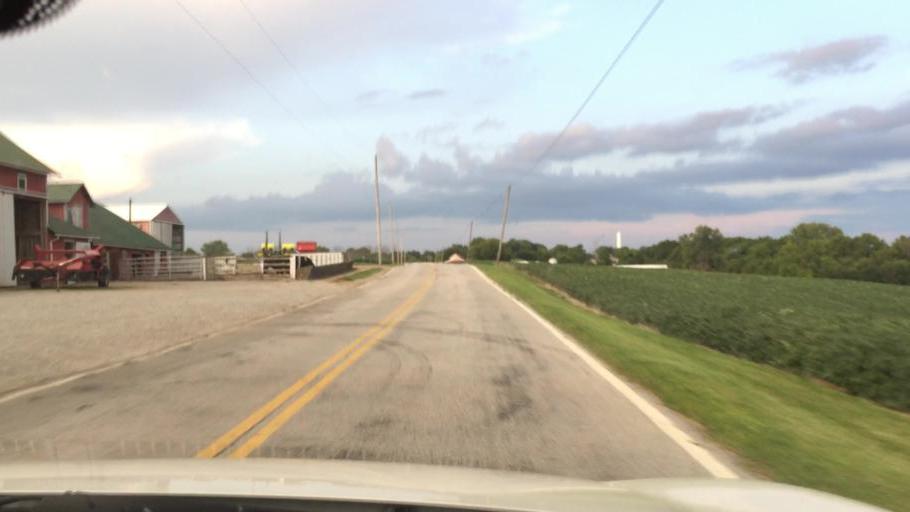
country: US
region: Ohio
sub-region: Champaign County
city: Mechanicsburg
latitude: 39.9970
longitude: -83.6347
